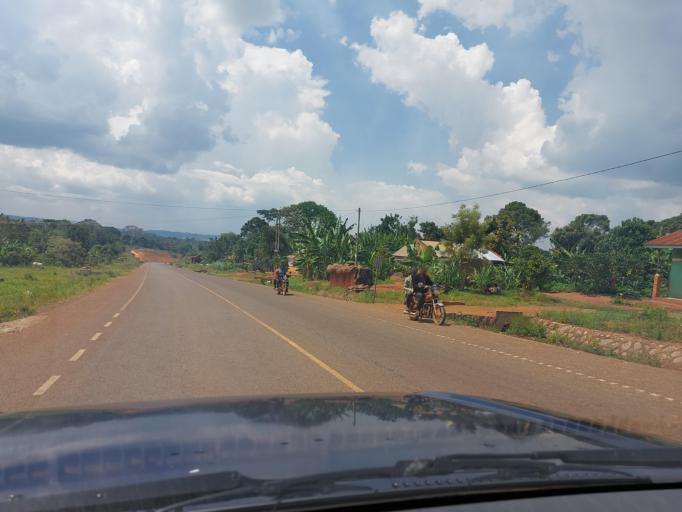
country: UG
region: Central Region
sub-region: Buikwe District
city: Buikwe
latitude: 0.2995
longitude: 33.0967
